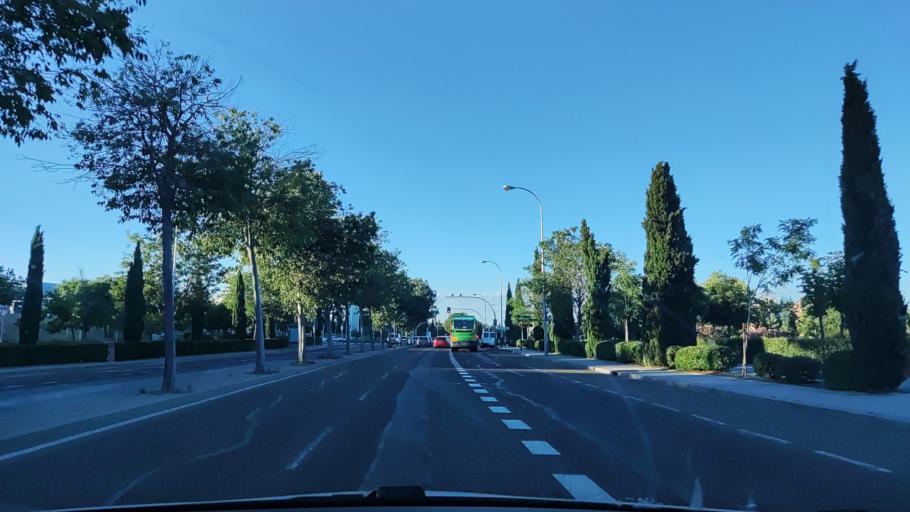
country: ES
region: Madrid
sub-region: Provincia de Madrid
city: Latina
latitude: 40.3665
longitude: -3.7418
